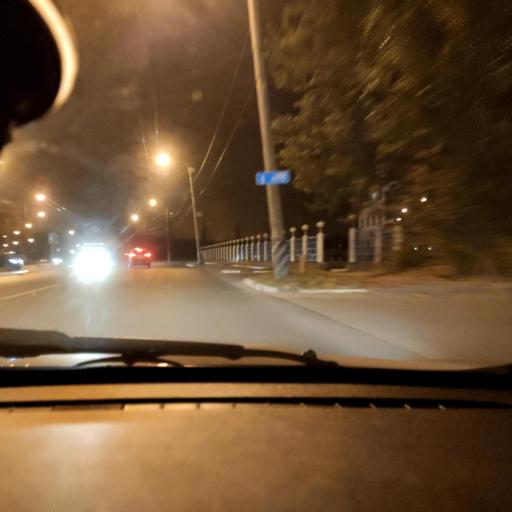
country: RU
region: Samara
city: Tol'yatti
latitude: 53.5011
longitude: 49.4232
